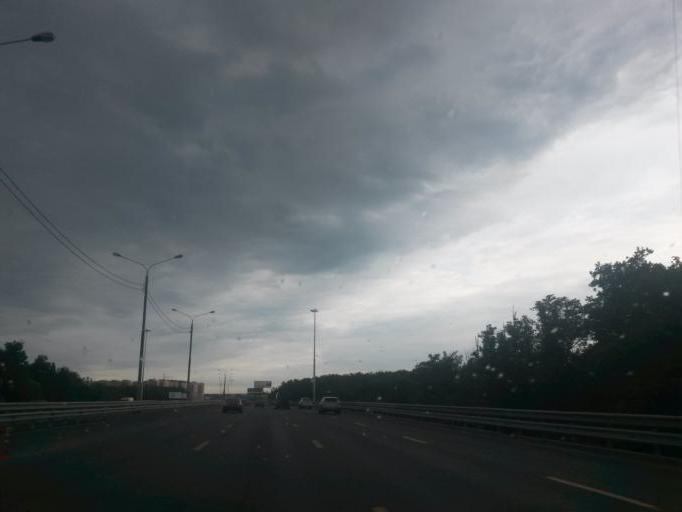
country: RU
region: Moscow
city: Annino
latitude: 55.5456
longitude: 37.6062
